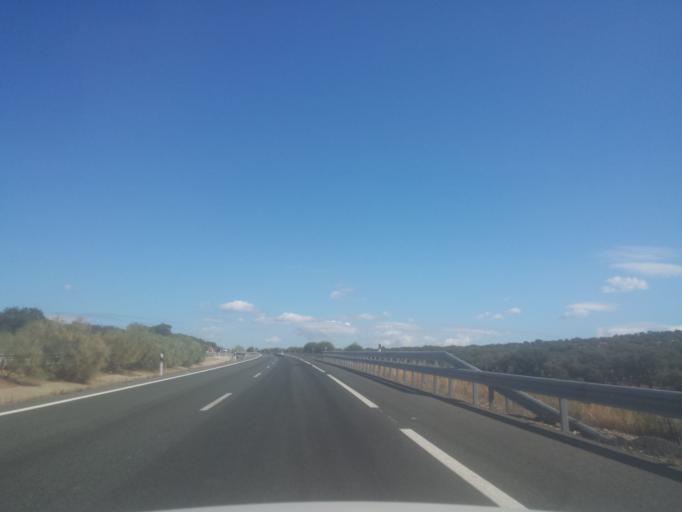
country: ES
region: Andalusia
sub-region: Provincia de Huelva
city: Santa Olalla del Cala
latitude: 37.8615
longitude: -6.2180
